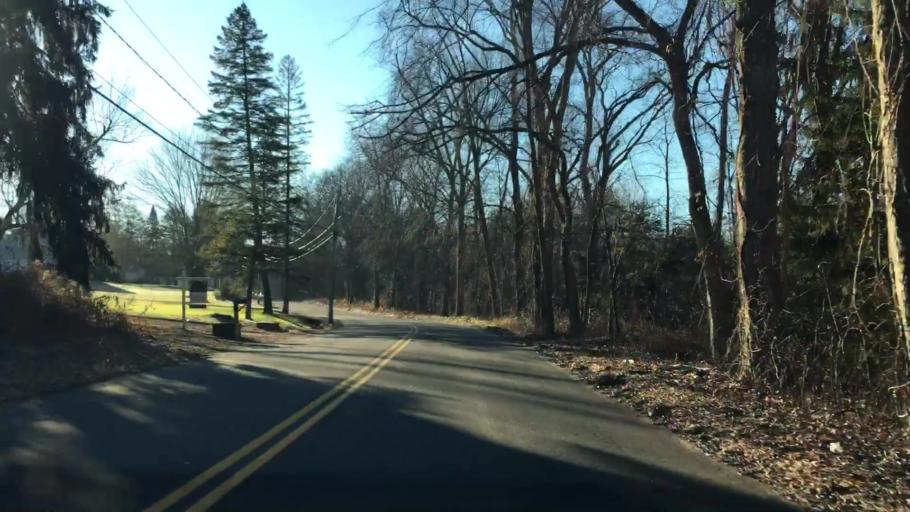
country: US
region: Connecticut
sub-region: New Haven County
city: Cheshire Village
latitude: 41.5539
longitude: -72.8695
